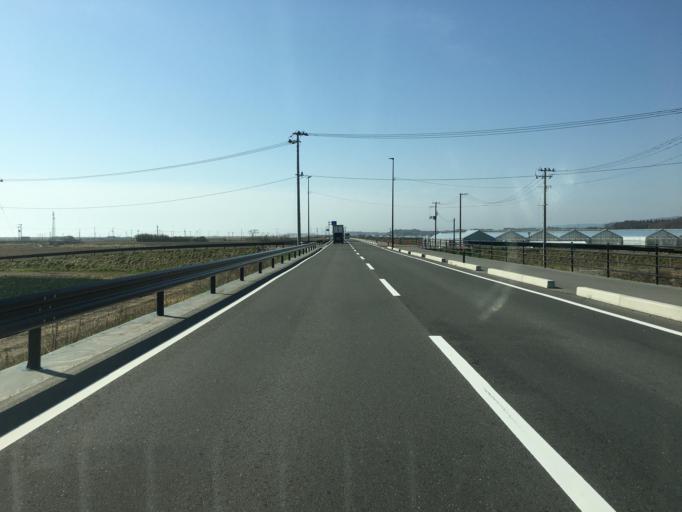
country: JP
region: Miyagi
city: Watari
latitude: 37.9474
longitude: 140.9070
